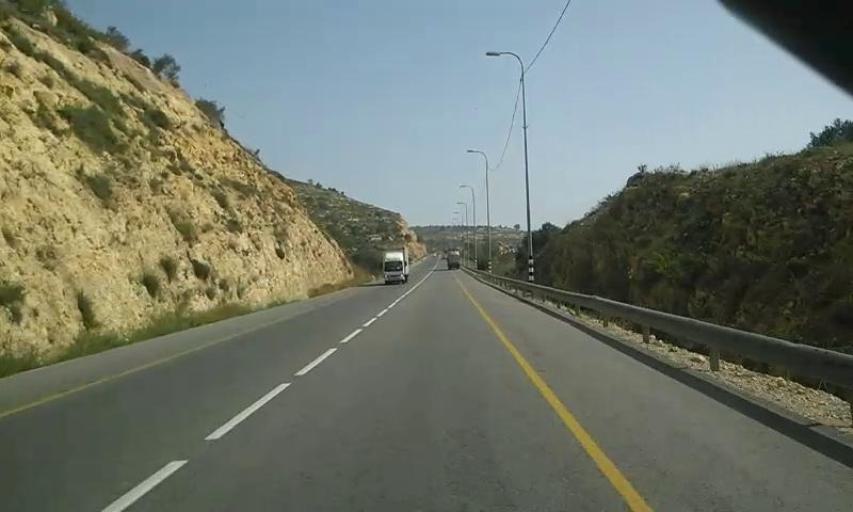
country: PS
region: West Bank
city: Yatma
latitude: 32.1073
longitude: 35.2560
